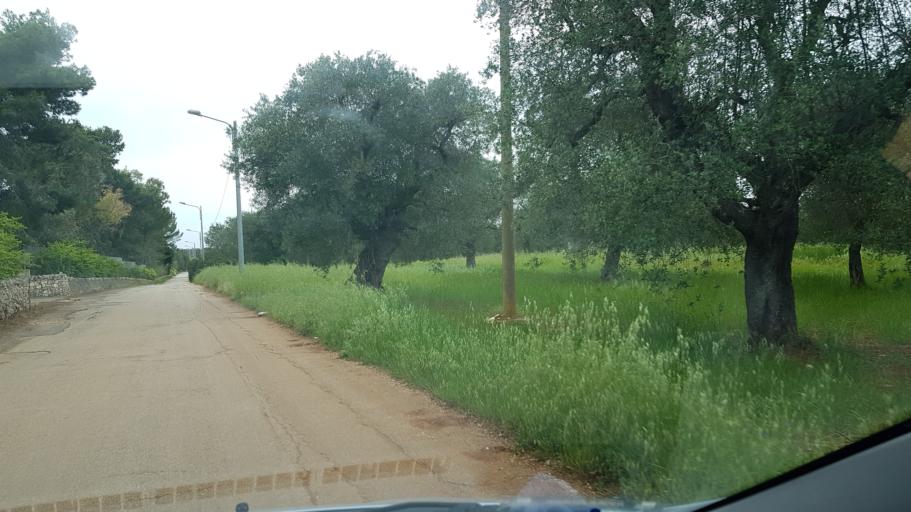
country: IT
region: Apulia
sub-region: Provincia di Brindisi
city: San Vito dei Normanni
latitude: 40.6641
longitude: 17.7348
